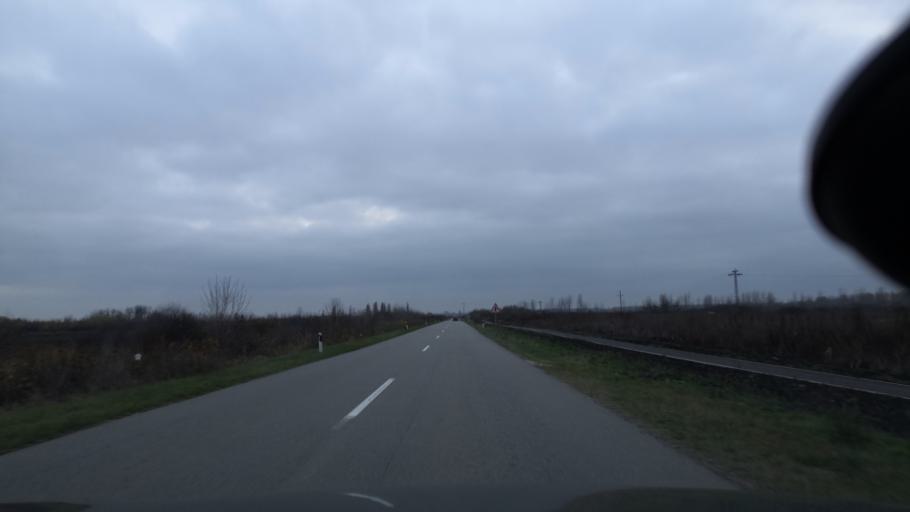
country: RS
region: Autonomna Pokrajina Vojvodina
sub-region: Severnobanatski Okrug
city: Novi Knezevac
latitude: 46.0831
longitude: 20.1063
